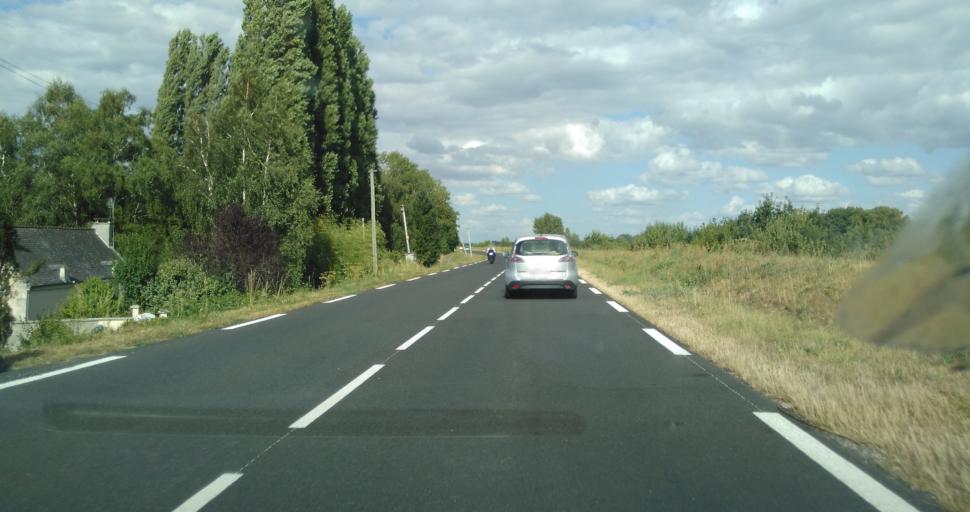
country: FR
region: Centre
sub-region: Departement d'Indre-et-Loire
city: La Chapelle-sur-Loire
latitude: 47.2526
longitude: 0.2369
